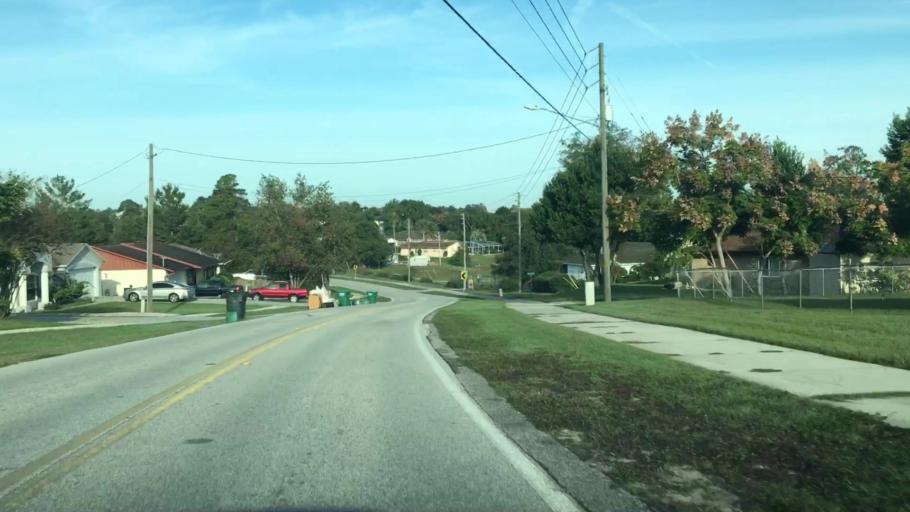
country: US
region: Florida
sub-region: Volusia County
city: Deltona
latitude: 28.9173
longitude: -81.2305
